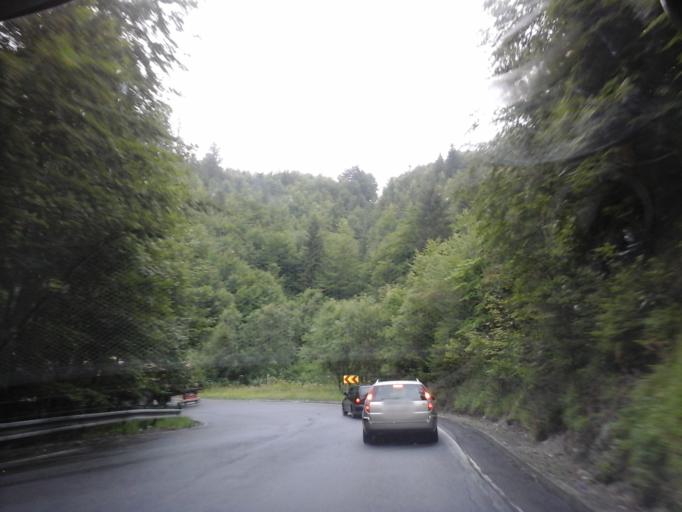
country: SK
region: Kosicky
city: Dobsina
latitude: 48.8975
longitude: 20.2465
